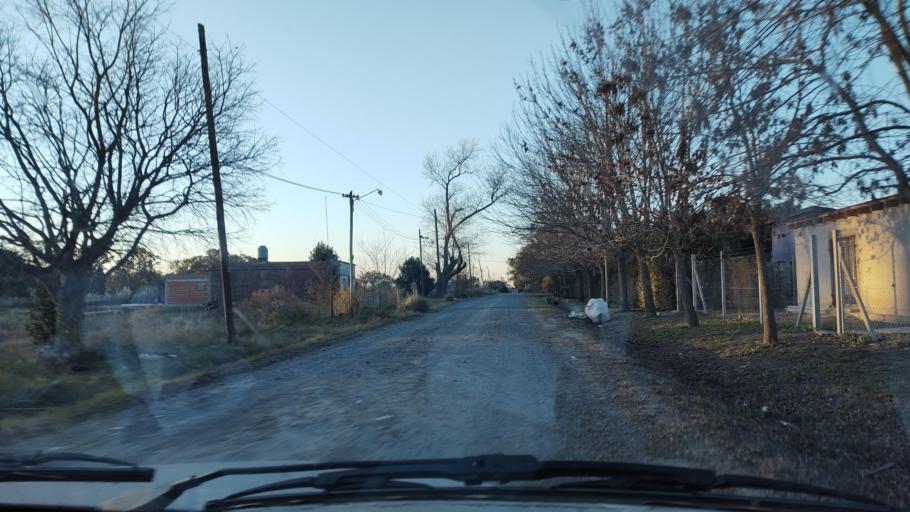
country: AR
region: Buenos Aires
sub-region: Partido de La Plata
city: La Plata
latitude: -34.9114
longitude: -58.0544
